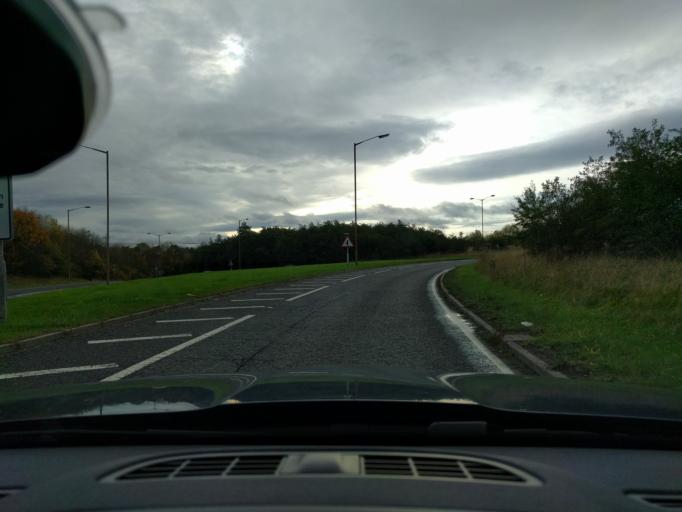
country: GB
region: England
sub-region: Northumberland
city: Bedlington
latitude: 55.1385
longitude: -1.5574
